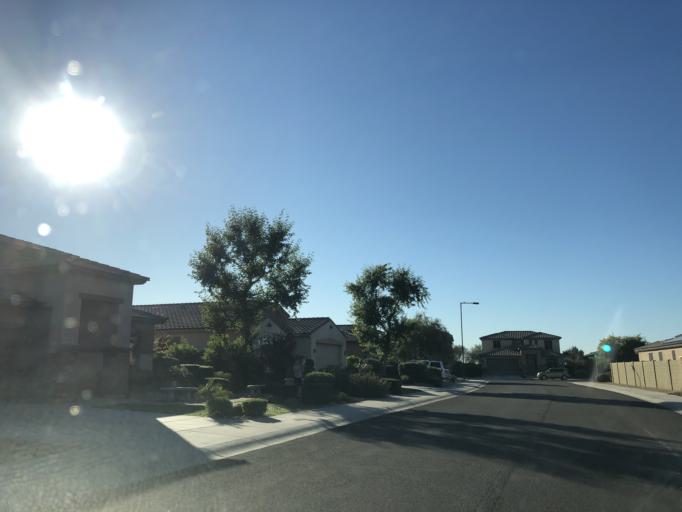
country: US
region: Arizona
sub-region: Maricopa County
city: Sun City West
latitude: 33.6906
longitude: -112.3254
